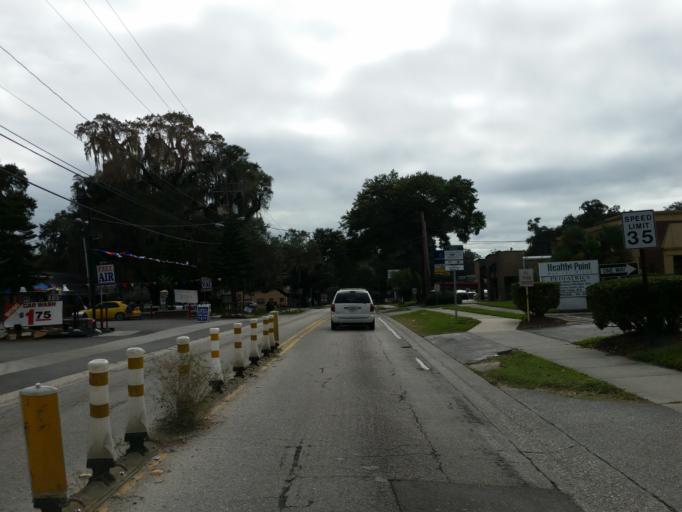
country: US
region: Florida
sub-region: Hillsborough County
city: Brandon
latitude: 27.9369
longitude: -82.2858
